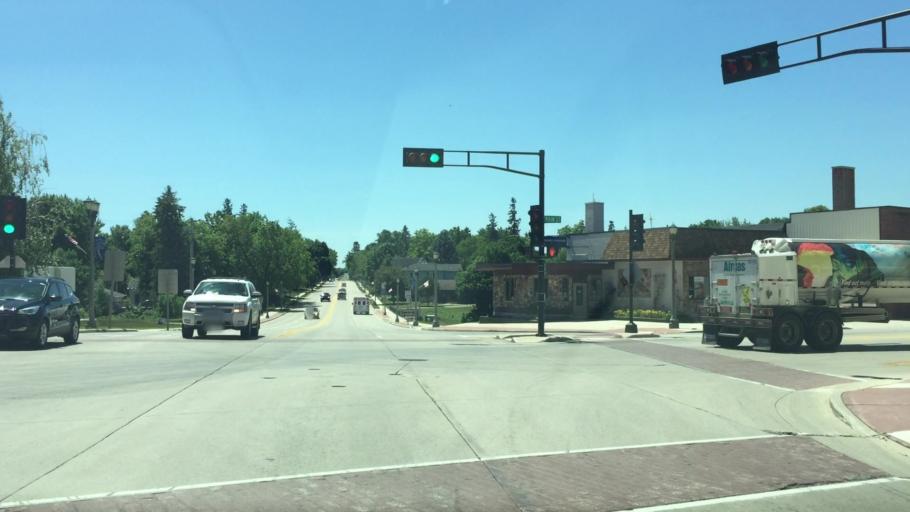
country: US
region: Wisconsin
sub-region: Calumet County
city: Chilton
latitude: 44.0289
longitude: -88.1629
